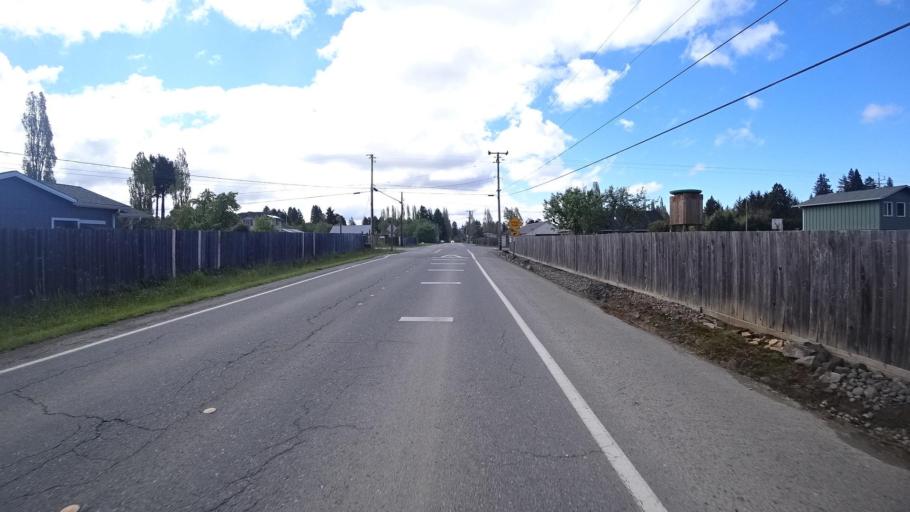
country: US
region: California
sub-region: Humboldt County
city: McKinleyville
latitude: 40.9675
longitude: -124.0359
